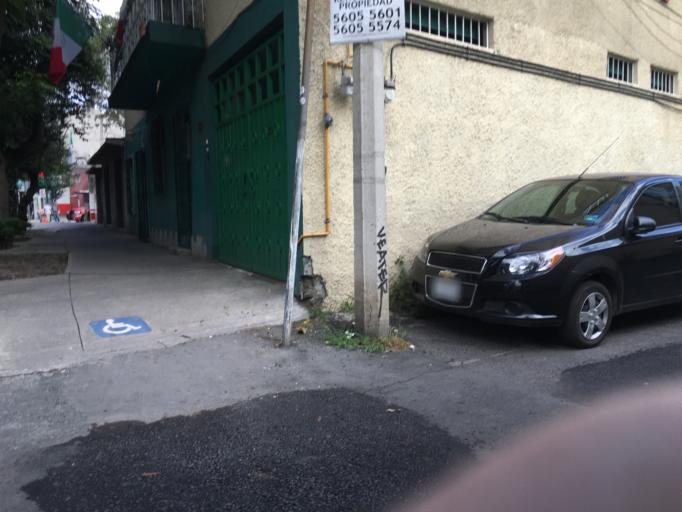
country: MX
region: Mexico City
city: Colonia Nativitas
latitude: 19.3726
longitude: -99.1474
